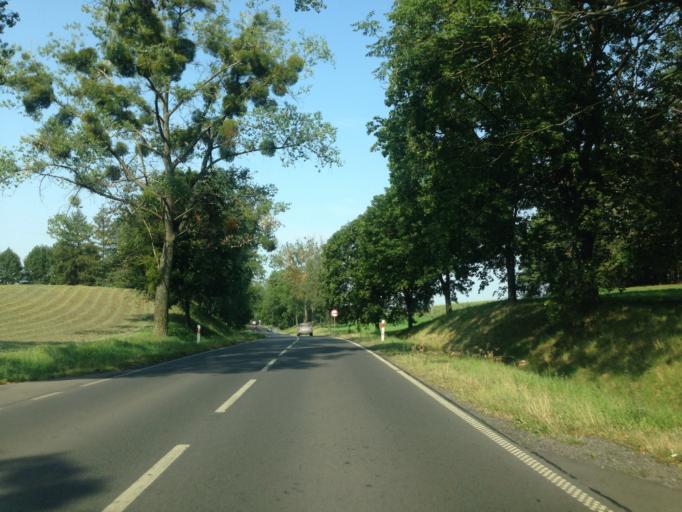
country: PL
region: Kujawsko-Pomorskie
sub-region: Powiat golubsko-dobrzynski
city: Golub-Dobrzyn
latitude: 53.1084
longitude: 19.1148
